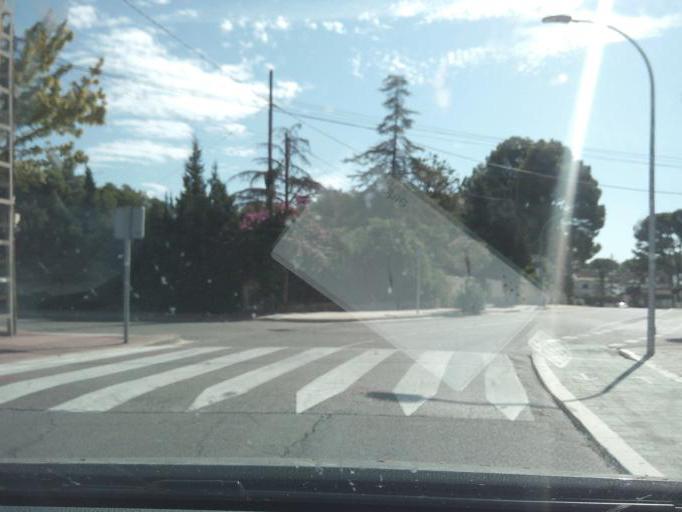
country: ES
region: Valencia
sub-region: Provincia de Valencia
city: Betera
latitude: 39.5415
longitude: -0.4826
